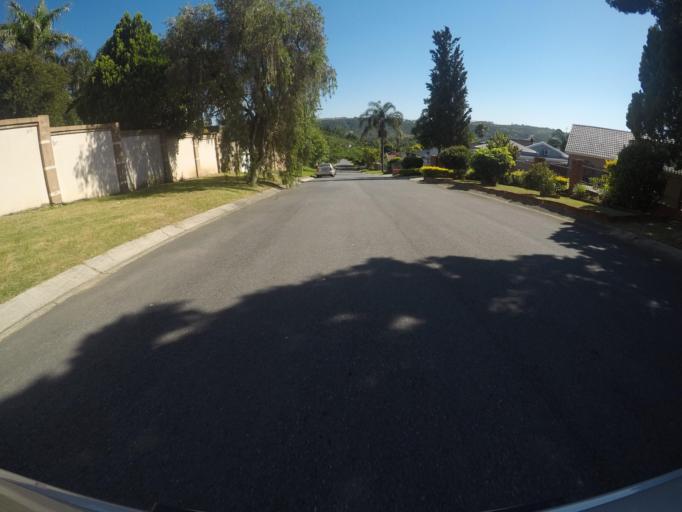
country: ZA
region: Eastern Cape
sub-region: Buffalo City Metropolitan Municipality
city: East London
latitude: -32.9530
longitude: 27.9003
